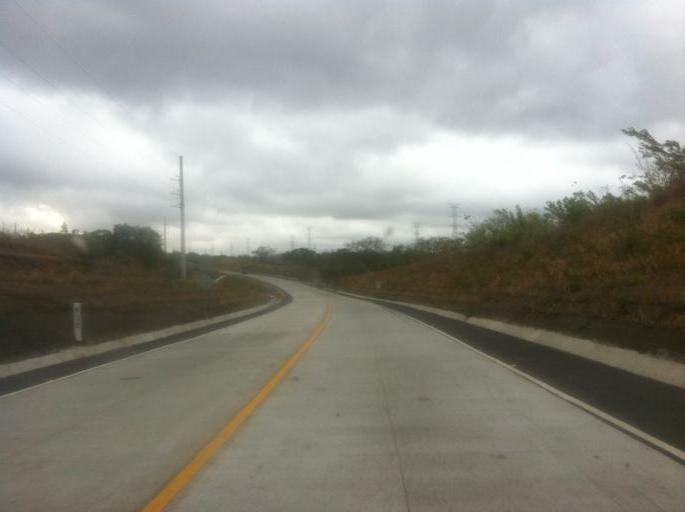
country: NI
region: Masaya
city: Masaya
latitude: 11.9880
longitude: -86.0731
